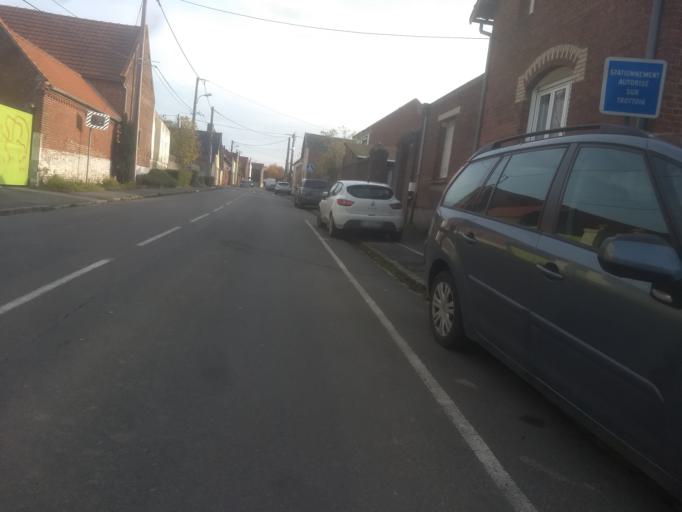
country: FR
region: Nord-Pas-de-Calais
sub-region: Departement du Pas-de-Calais
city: Agny
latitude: 50.2595
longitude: 2.7613
